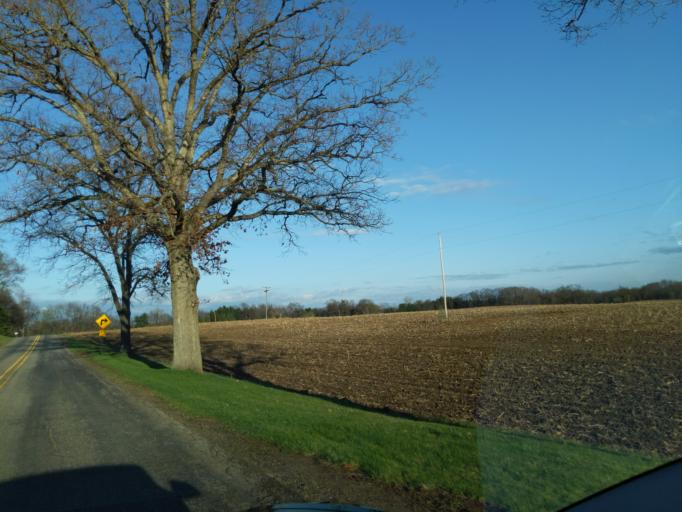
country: US
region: Michigan
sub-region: Ingham County
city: Leslie
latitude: 42.3458
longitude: -84.4591
